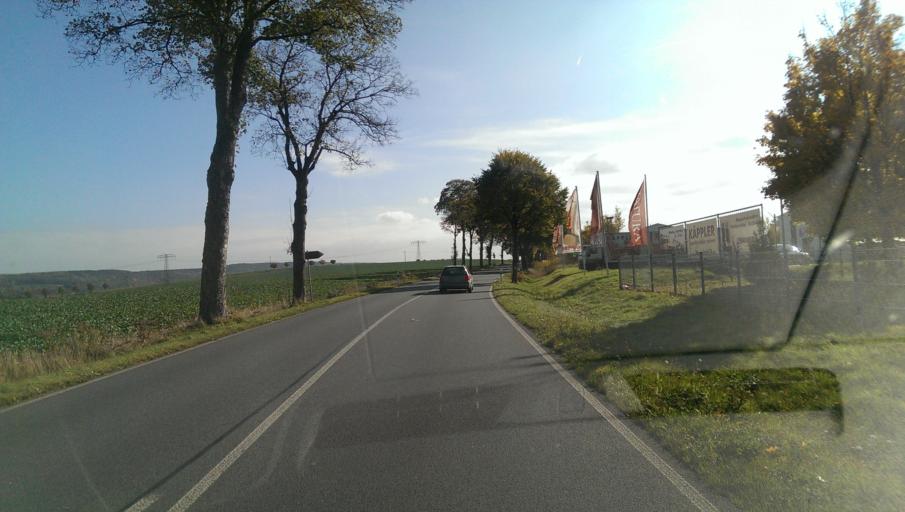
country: DE
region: Saxony
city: Dohma
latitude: 50.9226
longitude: 13.9354
